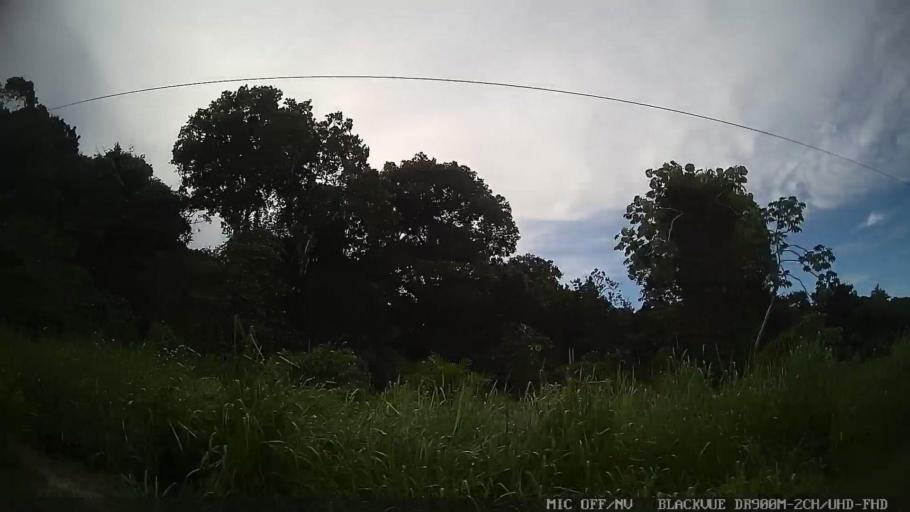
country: BR
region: Sao Paulo
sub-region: Iguape
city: Iguape
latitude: -24.6677
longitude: -47.4391
